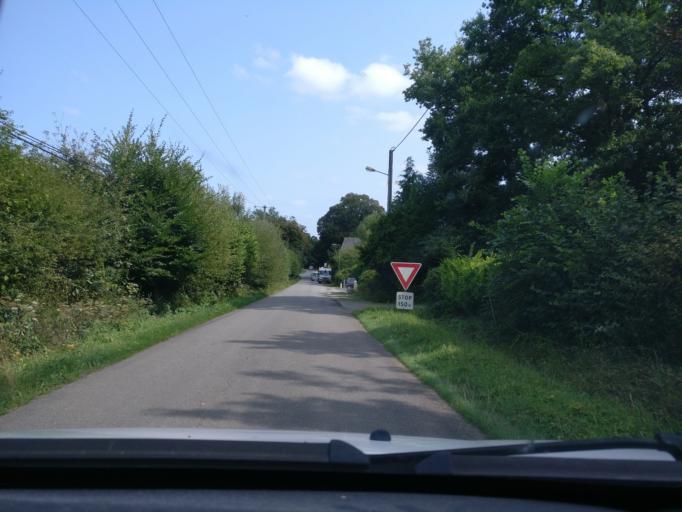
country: FR
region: Brittany
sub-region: Departement d'Ille-et-Vilaine
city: Erce-pres-Liffre
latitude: 48.2610
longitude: -1.5167
